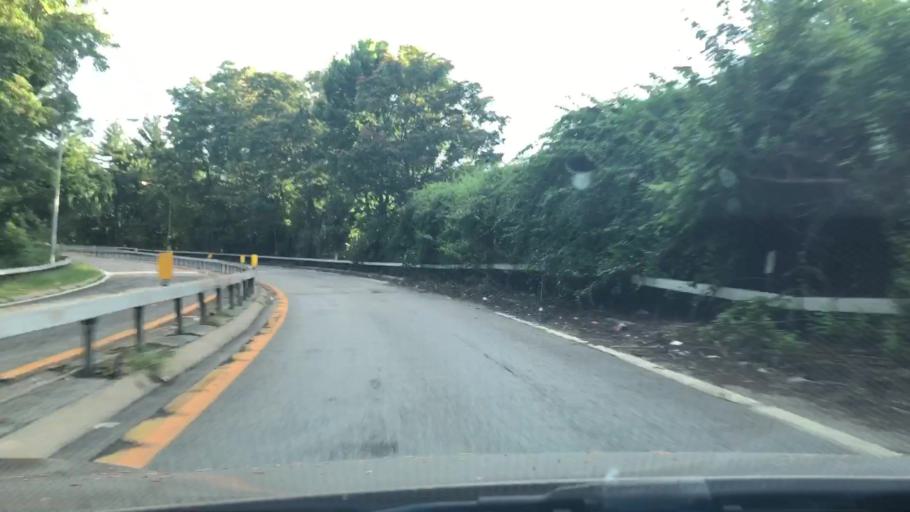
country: US
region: New York
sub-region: Westchester County
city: Mount Vernon
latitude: 40.9239
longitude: -73.8421
